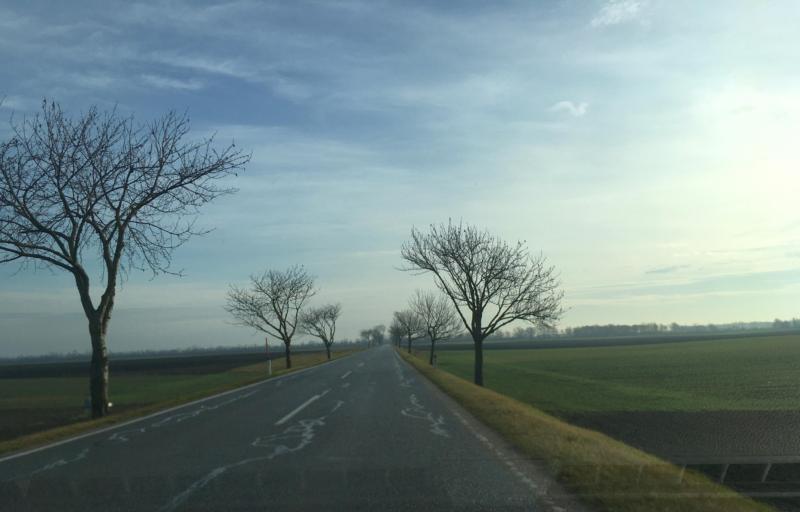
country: AT
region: Lower Austria
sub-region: Politischer Bezirk Ganserndorf
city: Raasdorf
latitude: 48.2126
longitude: 16.6006
